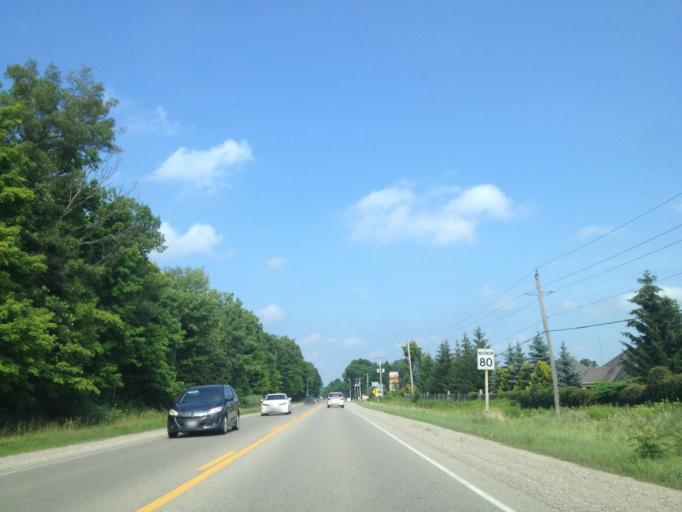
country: CA
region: Ontario
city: Delaware
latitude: 42.9616
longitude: -81.4030
